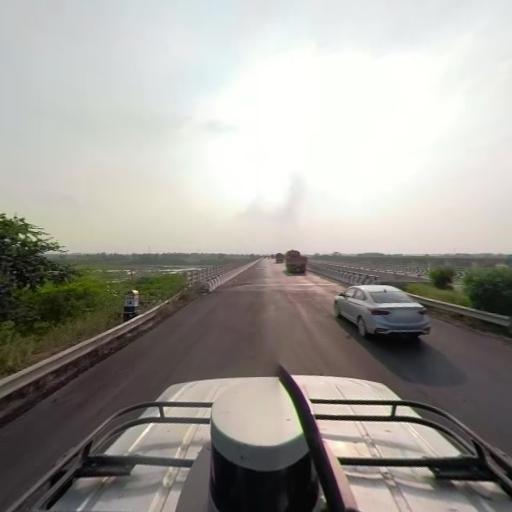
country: IN
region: Telangana
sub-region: Nalgonda
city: Suriapet
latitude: 17.1631
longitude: 79.5214
